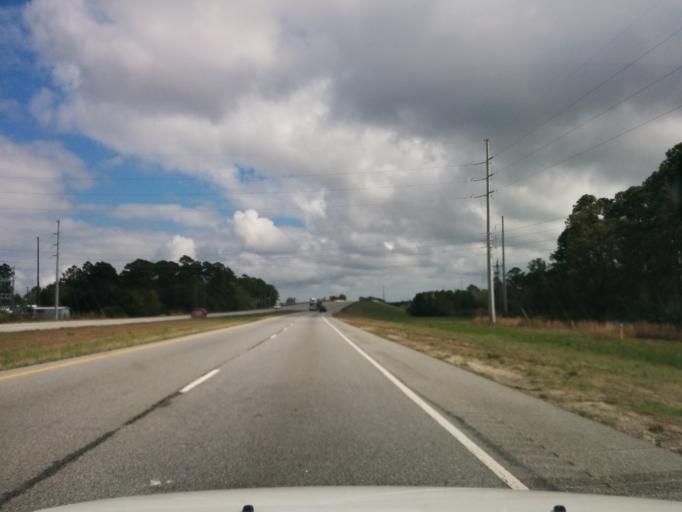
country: US
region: Georgia
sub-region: Glynn County
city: Brunswick
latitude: 31.1238
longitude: -81.5472
